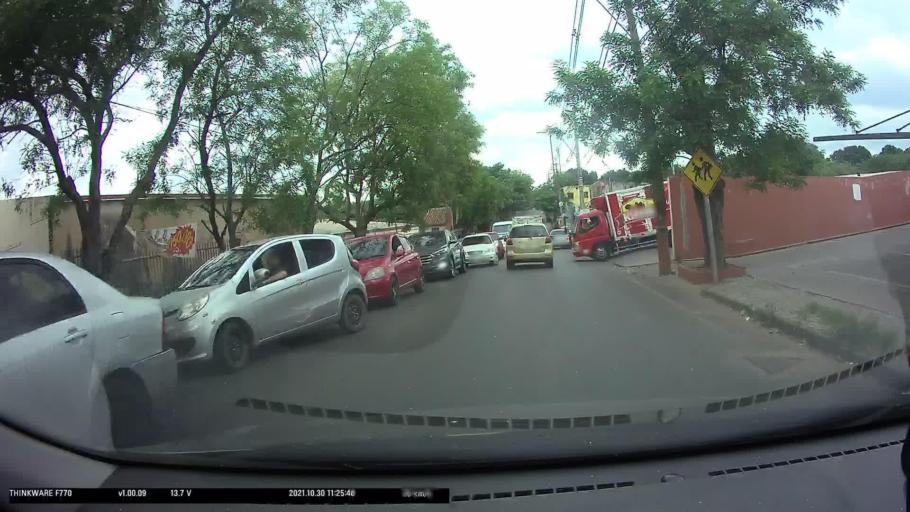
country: PY
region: Central
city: Fernando de la Mora
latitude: -25.3217
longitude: -57.5245
